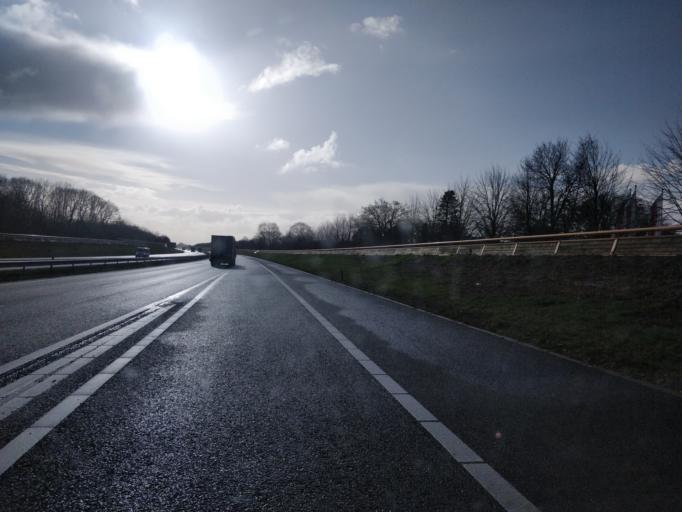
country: NL
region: Friesland
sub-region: Gemeente Heerenveen
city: Oranjewoud
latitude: 52.9489
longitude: 5.9438
